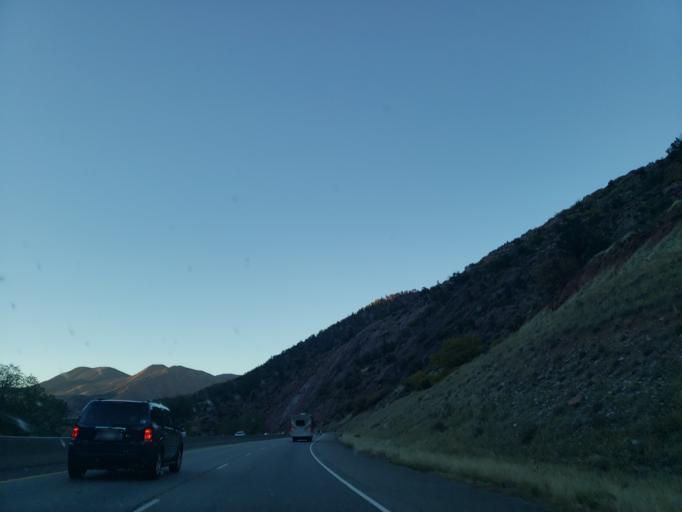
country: US
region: Colorado
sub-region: Garfield County
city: Glenwood Springs
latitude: 39.5682
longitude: -107.4262
